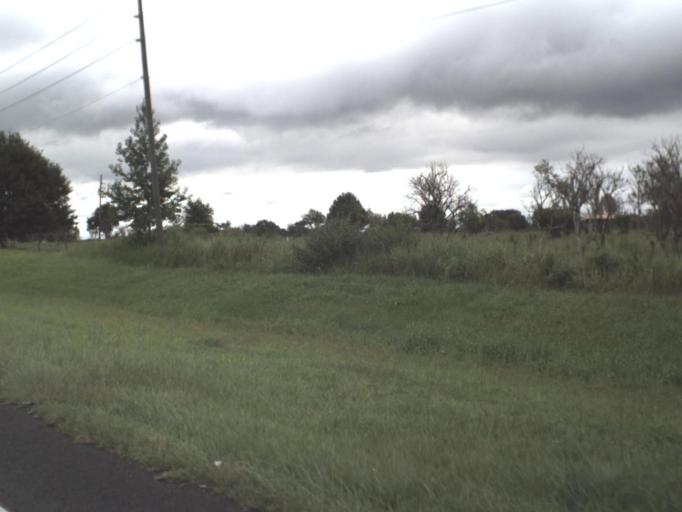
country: US
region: Florida
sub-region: Hardee County
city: Bowling Green
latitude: 27.5957
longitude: -81.8221
